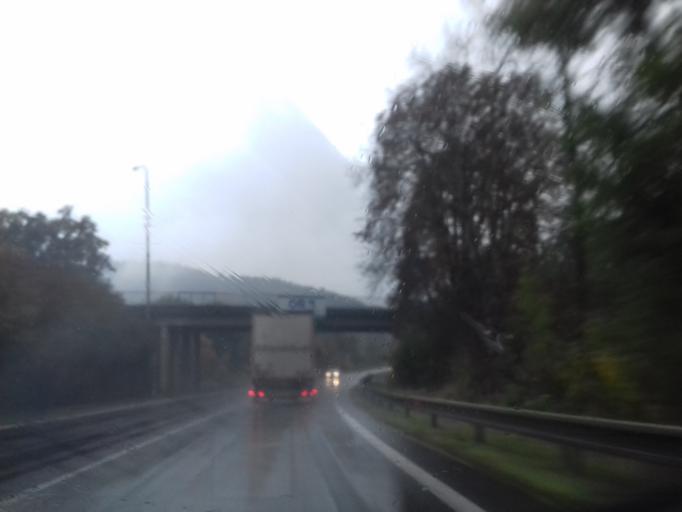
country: CZ
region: Pardubicky
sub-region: Okres Svitavy
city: Moravska Trebova
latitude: 49.7566
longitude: 16.6683
